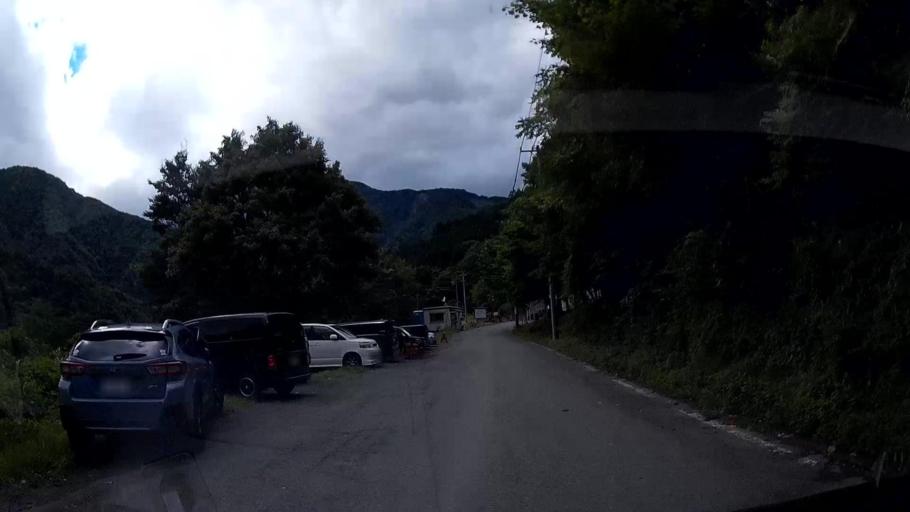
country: JP
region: Nagano
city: Iida
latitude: 35.3297
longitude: 138.1799
